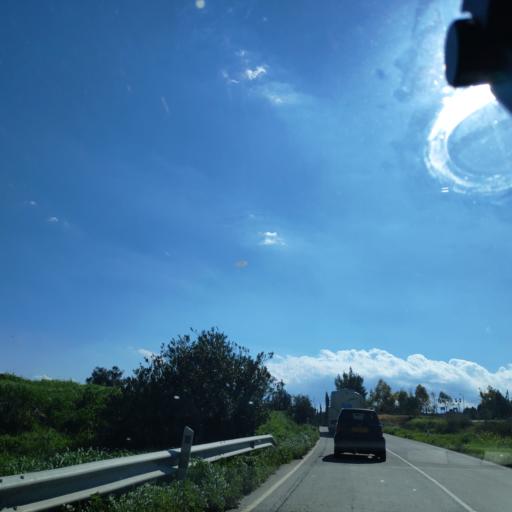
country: CY
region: Lefkosia
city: Tseri
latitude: 35.0256
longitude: 33.3273
